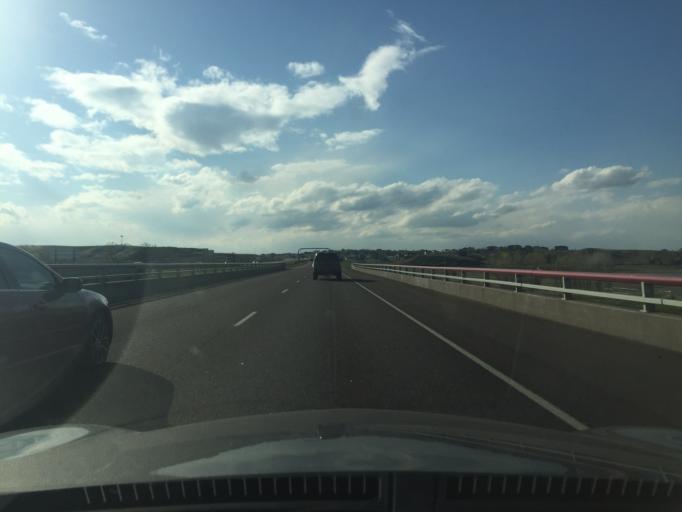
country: US
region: Colorado
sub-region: Adams County
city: Todd Creek
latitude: 39.9474
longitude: -104.8592
